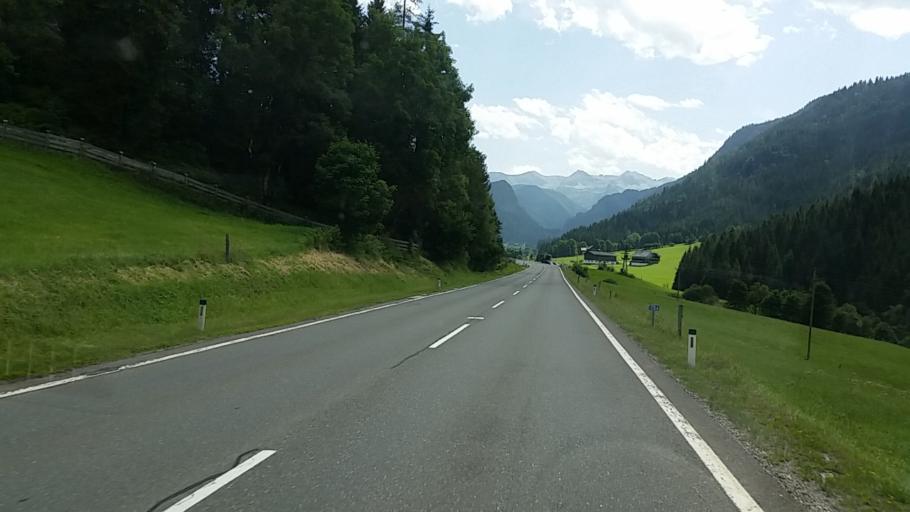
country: AT
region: Salzburg
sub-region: Politischer Bezirk Sankt Johann im Pongau
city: Untertauern
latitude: 47.3393
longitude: 13.5044
